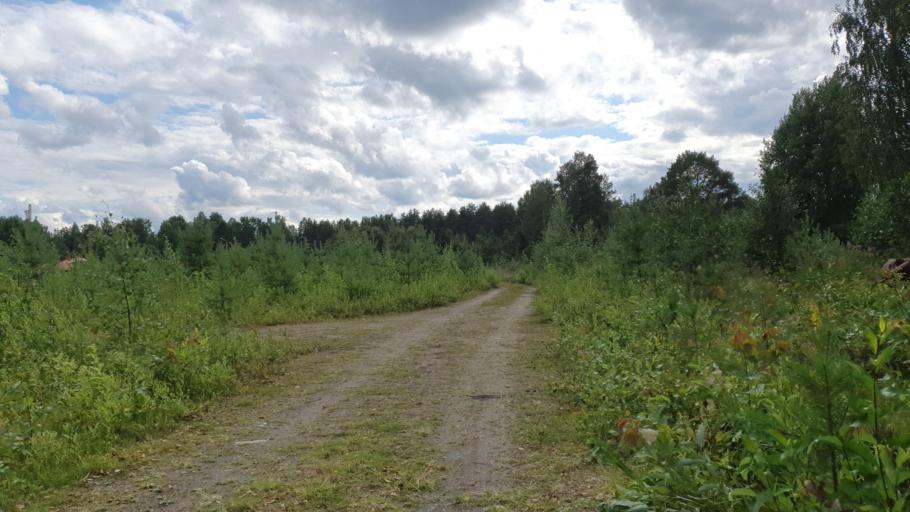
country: FI
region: Kainuu
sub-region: Kehys-Kainuu
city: Kuhmo
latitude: 64.1346
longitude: 29.5270
